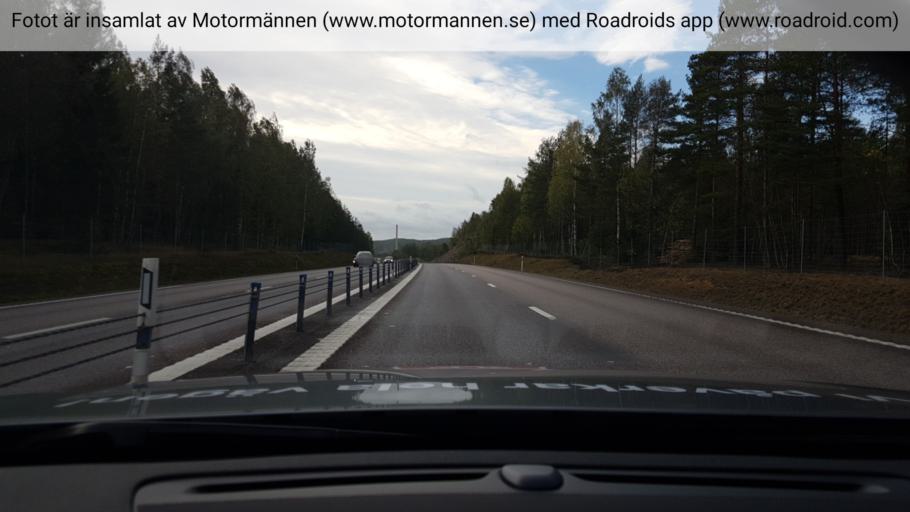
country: SE
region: Vaermland
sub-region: Karlstads Kommun
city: Valberg
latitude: 59.3824
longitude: 13.2108
